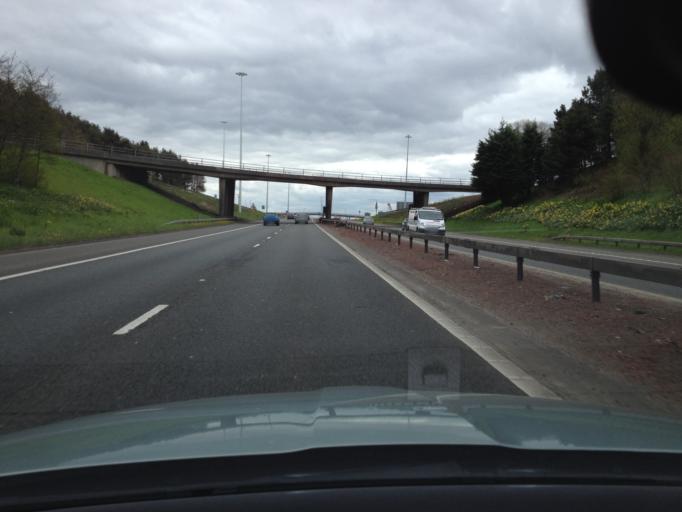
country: GB
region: Scotland
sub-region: South Lanarkshire
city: Uddingston
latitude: 55.8529
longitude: -4.0895
